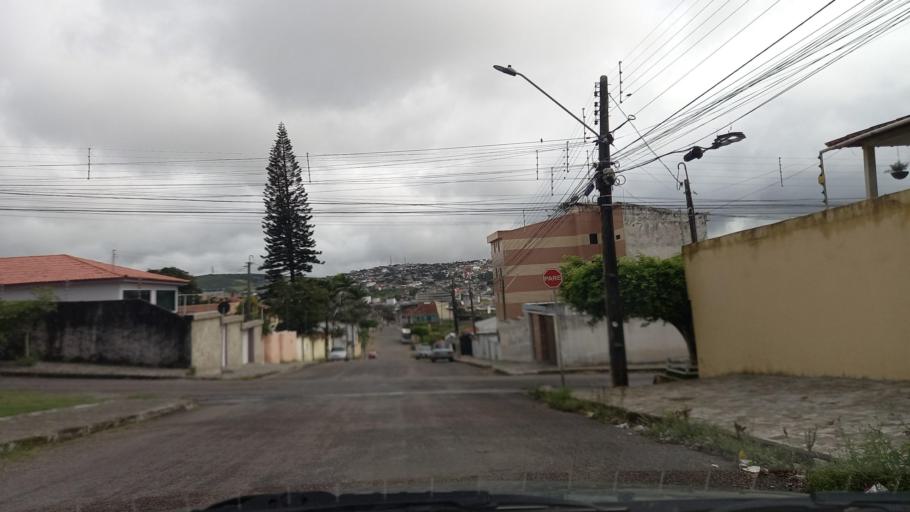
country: BR
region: Pernambuco
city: Garanhuns
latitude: -8.9013
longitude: -36.4917
